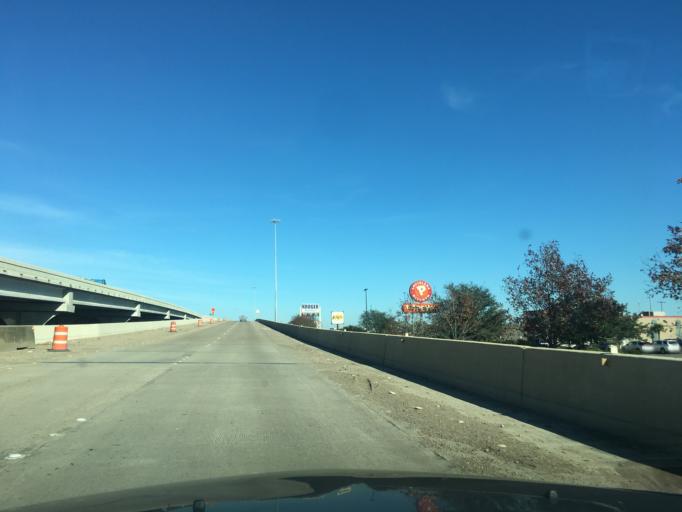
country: US
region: Texas
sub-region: Fort Bend County
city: Richmond
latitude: 29.5450
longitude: -95.7497
